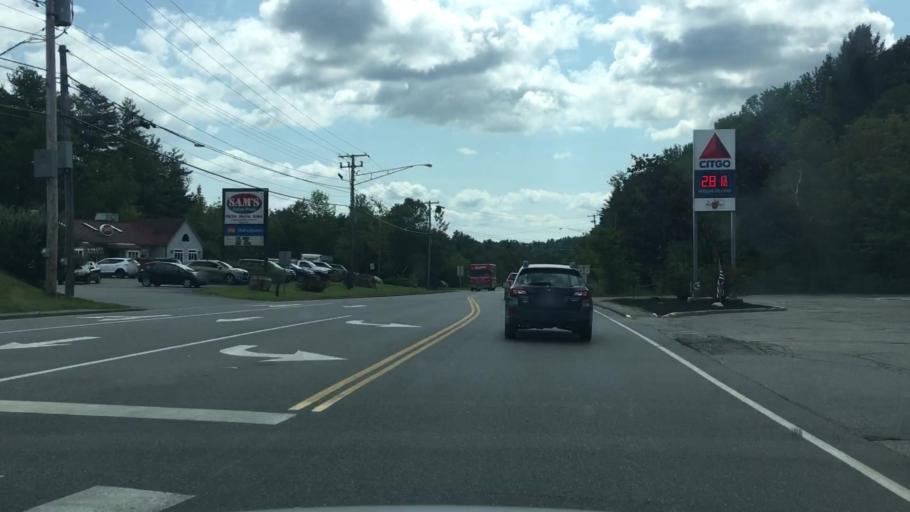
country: US
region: Maine
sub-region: Kennebec County
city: Augusta
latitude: 44.3399
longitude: -69.7925
